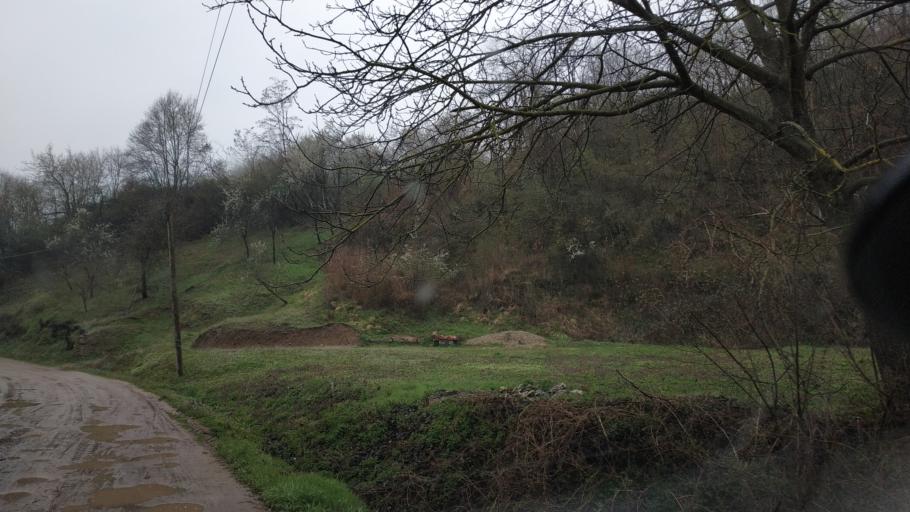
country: RS
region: Central Serbia
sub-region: Zajecarski Okrug
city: Soko Banja
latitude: 43.5744
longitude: 21.8052
